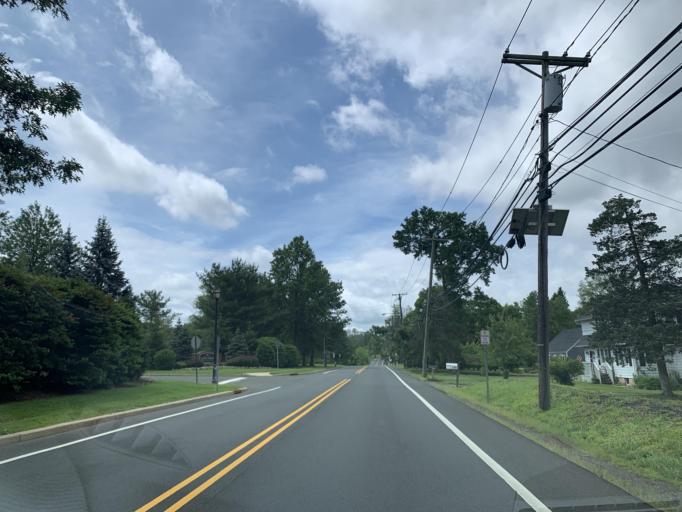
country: US
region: New Jersey
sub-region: Somerset County
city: Martinsville
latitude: 40.5958
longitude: -74.5613
